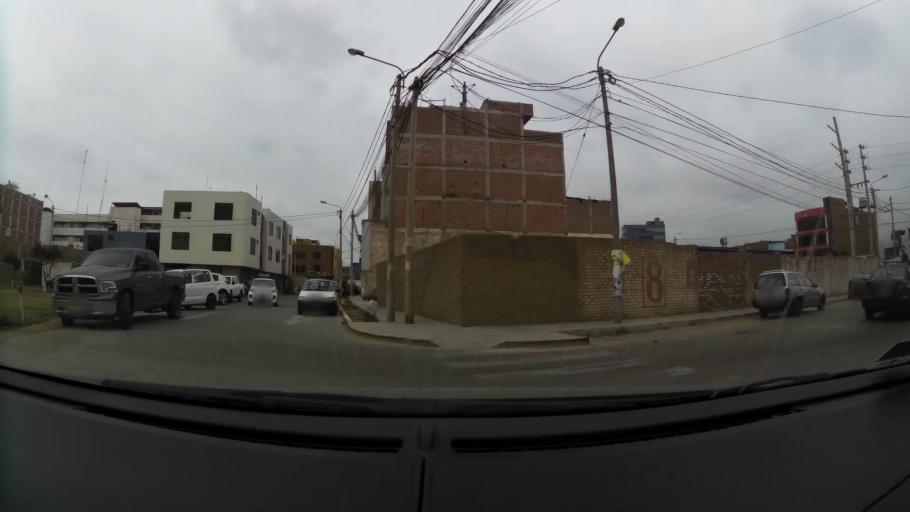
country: PE
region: La Libertad
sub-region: Provincia de Trujillo
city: Trujillo
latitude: -8.1142
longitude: -79.0475
